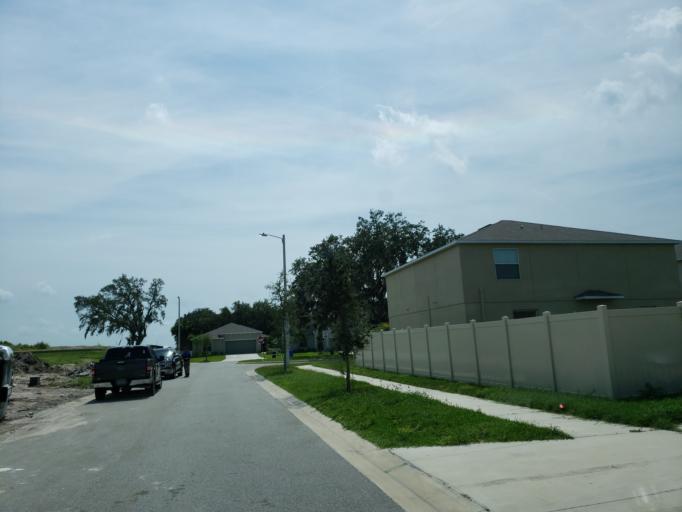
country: US
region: Florida
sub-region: Hillsborough County
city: Riverview
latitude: 27.8474
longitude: -82.3393
